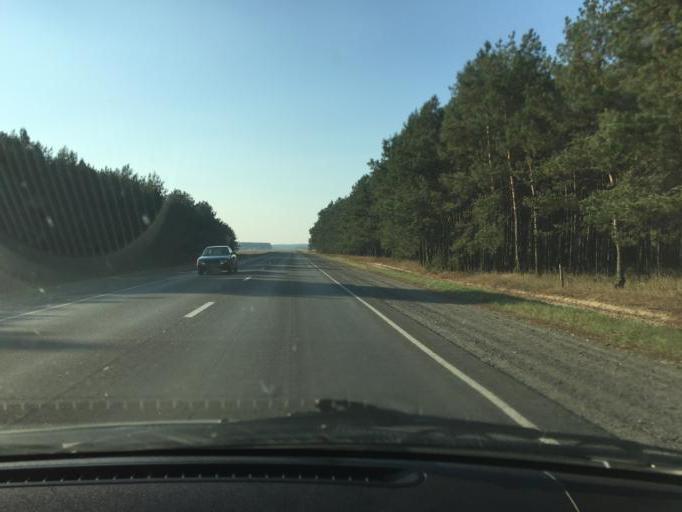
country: BY
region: Brest
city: Davyd-Haradok
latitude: 52.2391
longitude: 27.2134
